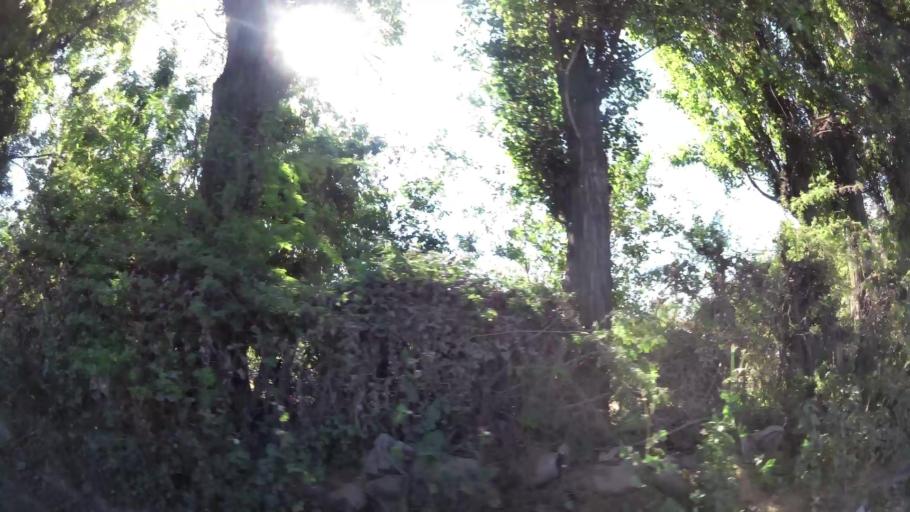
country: CL
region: Santiago Metropolitan
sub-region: Provincia de Maipo
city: San Bernardo
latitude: -33.5575
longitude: -70.7710
